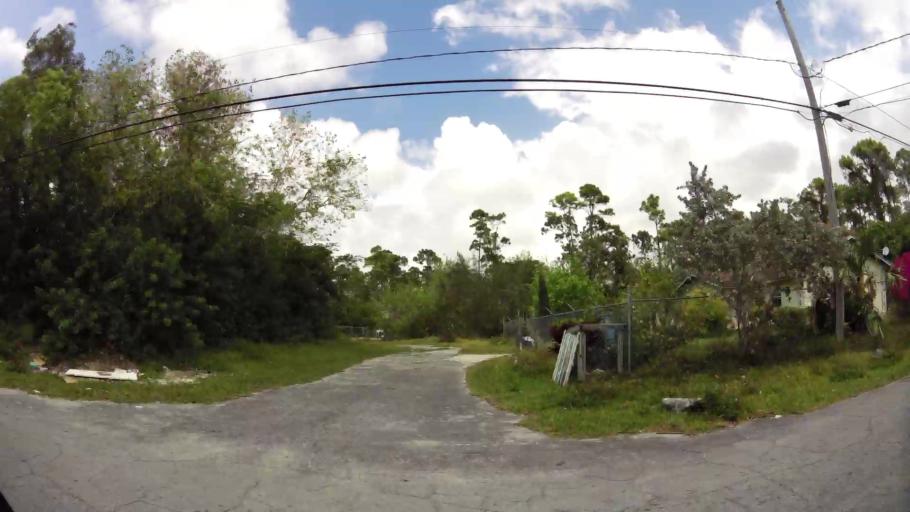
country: BS
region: Freeport
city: Lucaya
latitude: 26.5268
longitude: -78.6572
